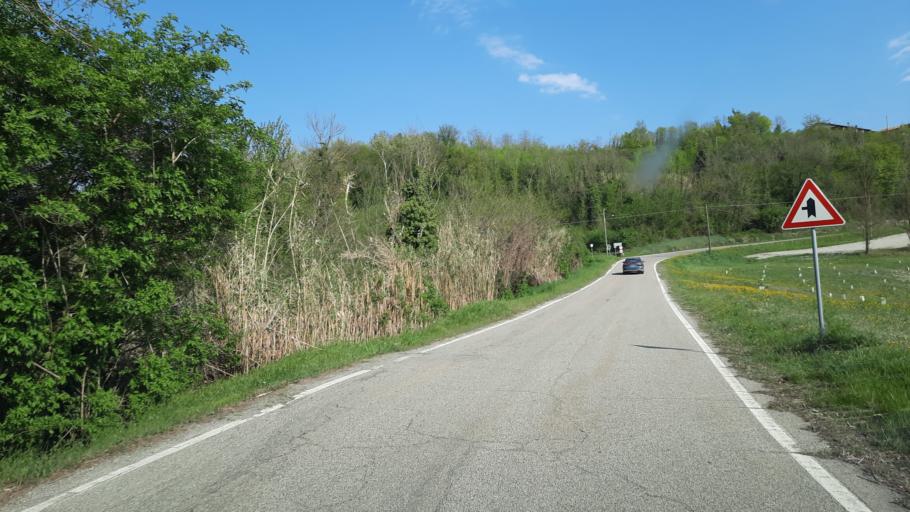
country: IT
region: Piedmont
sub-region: Provincia di Alessandria
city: Villamiroglio
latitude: 45.1390
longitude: 8.1698
